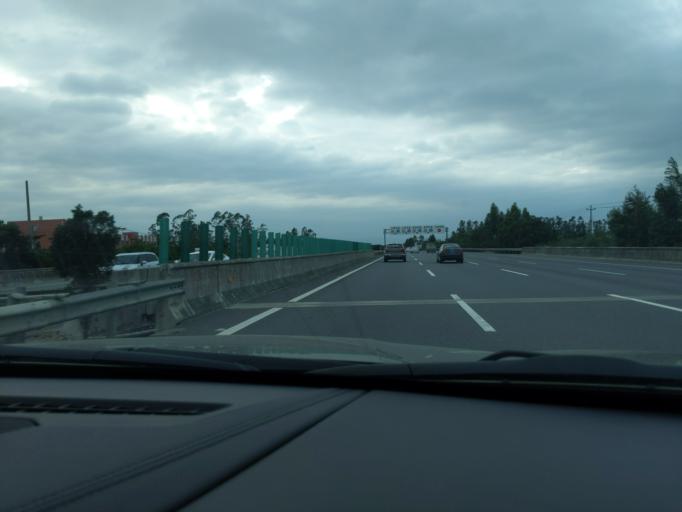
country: CN
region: Fujian
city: Maxiang
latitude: 24.6807
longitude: 118.2879
